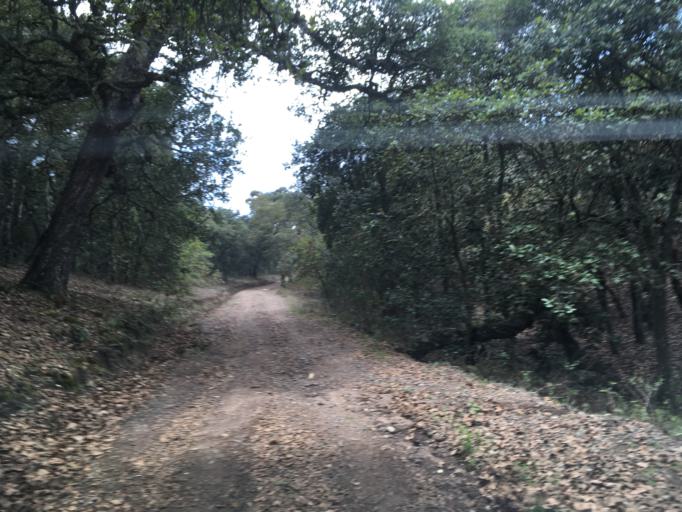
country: MX
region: Oaxaca
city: San Andres Sinaxtla
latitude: 17.6060
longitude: -97.2646
